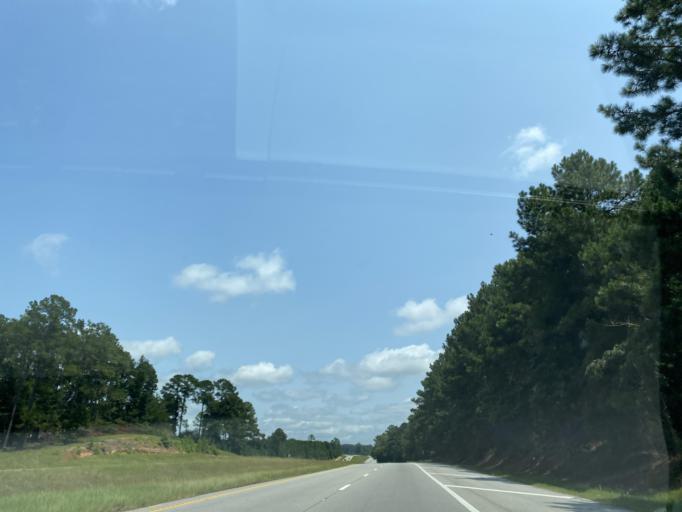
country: US
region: Georgia
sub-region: Telfair County
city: Lumber City
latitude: 31.9050
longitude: -82.6543
